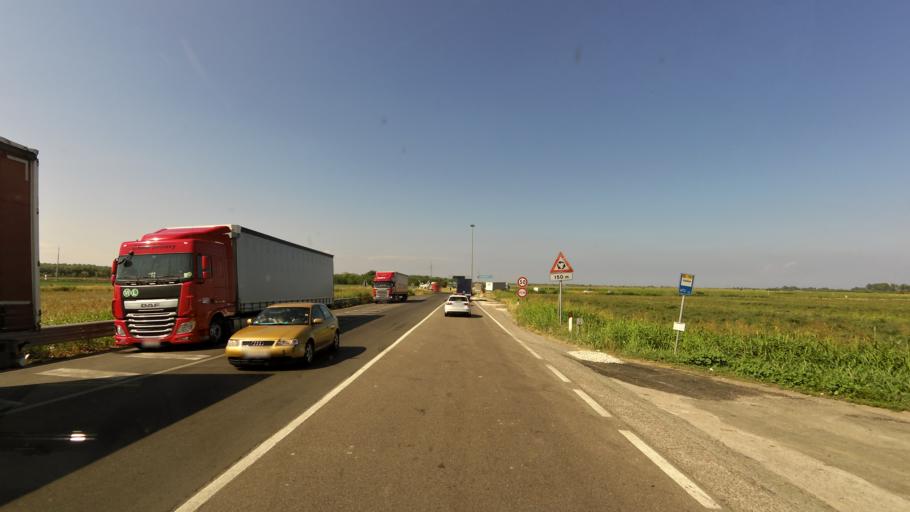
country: IT
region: Emilia-Romagna
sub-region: Provincia di Ravenna
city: Marina Romea
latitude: 44.5642
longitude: 12.2501
